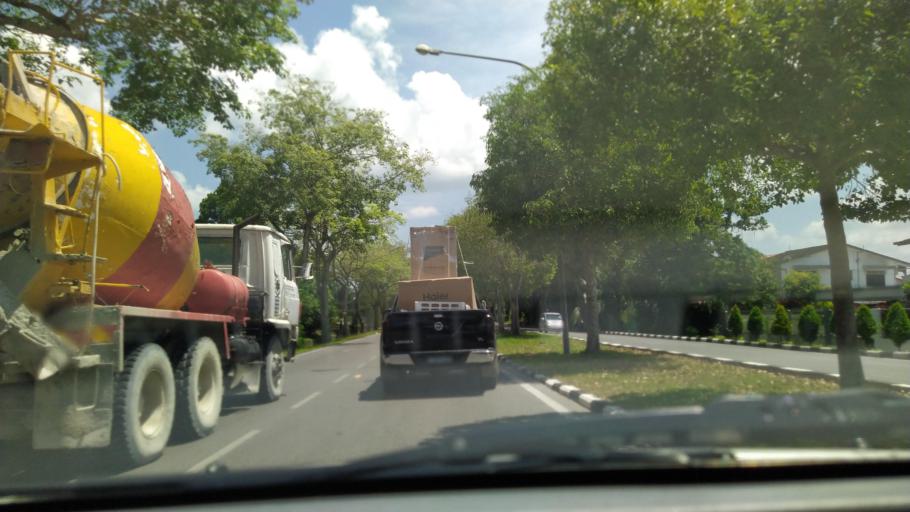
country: MY
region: Sarawak
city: Sibu
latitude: 2.3041
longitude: 111.8324
